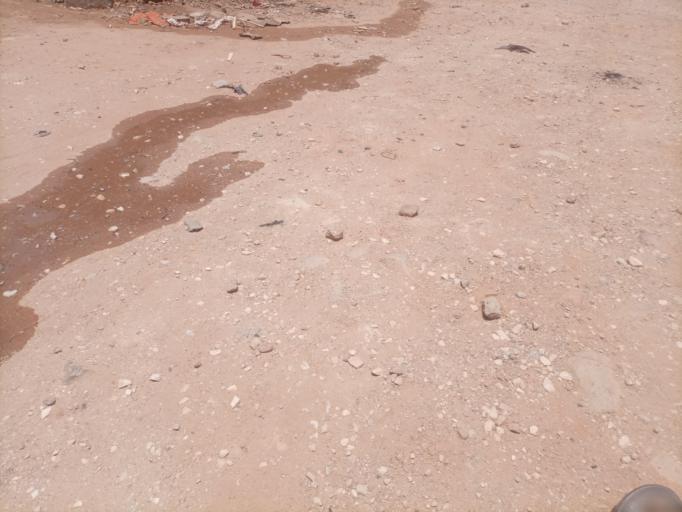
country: ZM
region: Lusaka
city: Lusaka
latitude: -15.4083
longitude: 28.3713
